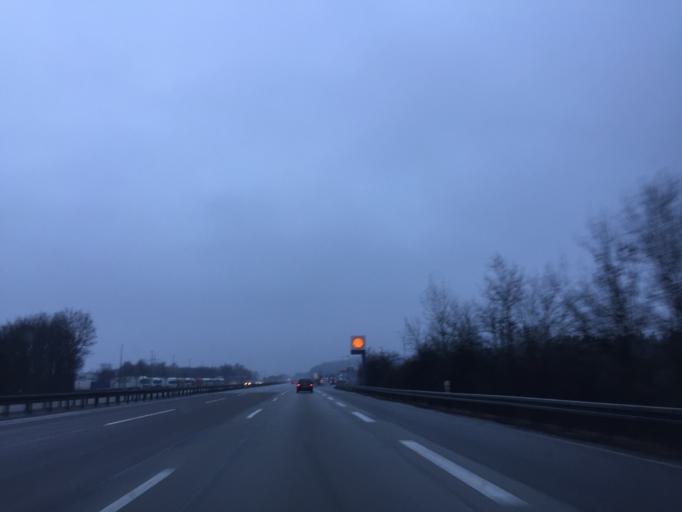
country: DE
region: Hesse
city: Bad Camberg
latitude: 50.3040
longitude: 8.2339
